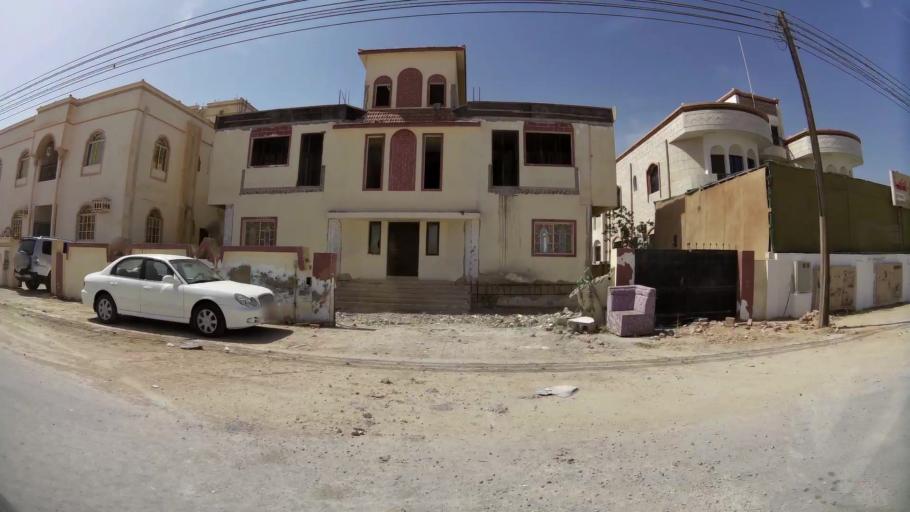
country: OM
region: Zufar
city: Salalah
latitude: 17.0445
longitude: 54.1588
